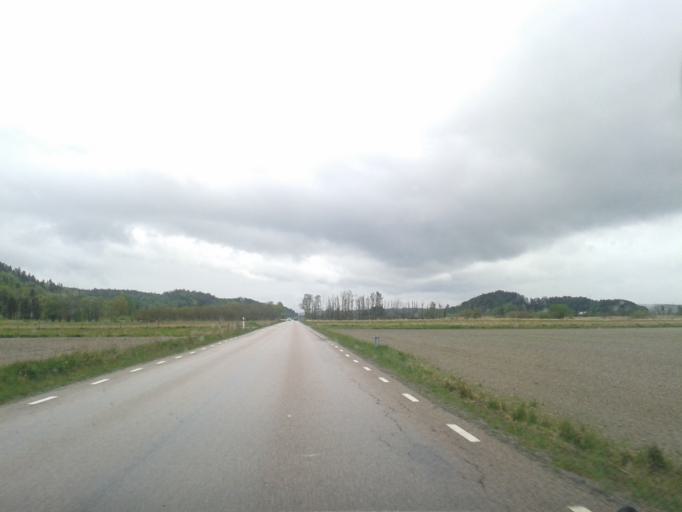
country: SE
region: Vaestra Goetaland
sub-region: Ale Kommun
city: Alvangen
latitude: 57.9900
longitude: 12.1175
